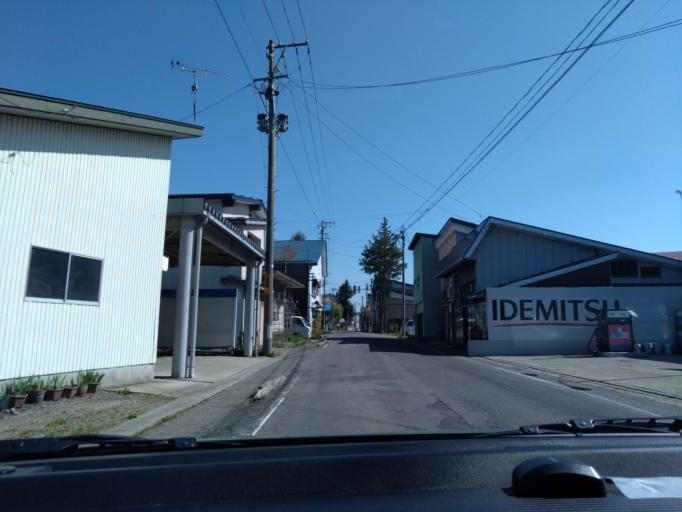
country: JP
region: Akita
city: Kakunodatemachi
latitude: 39.5586
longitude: 140.5852
